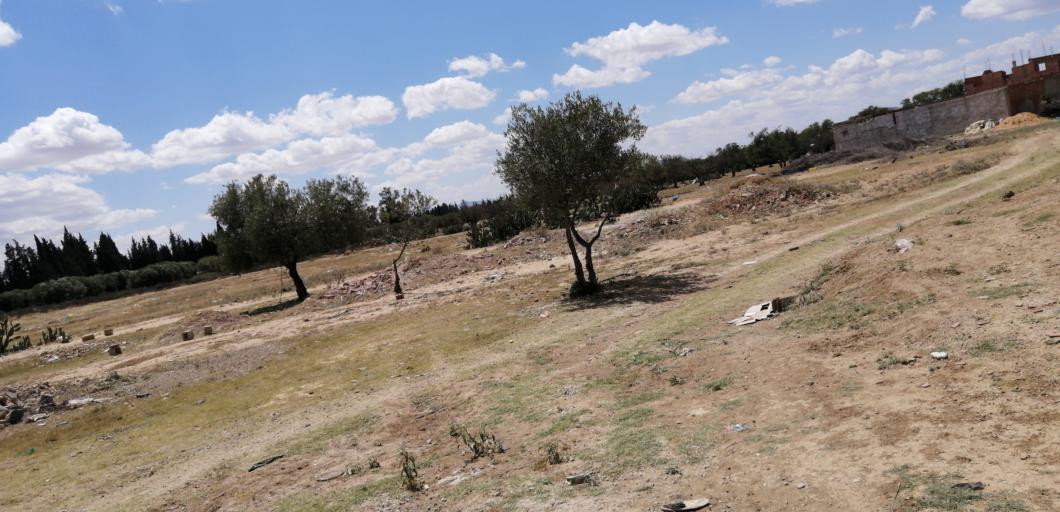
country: TN
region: Al Qayrawan
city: Kairouan
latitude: 35.6165
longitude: 9.9233
